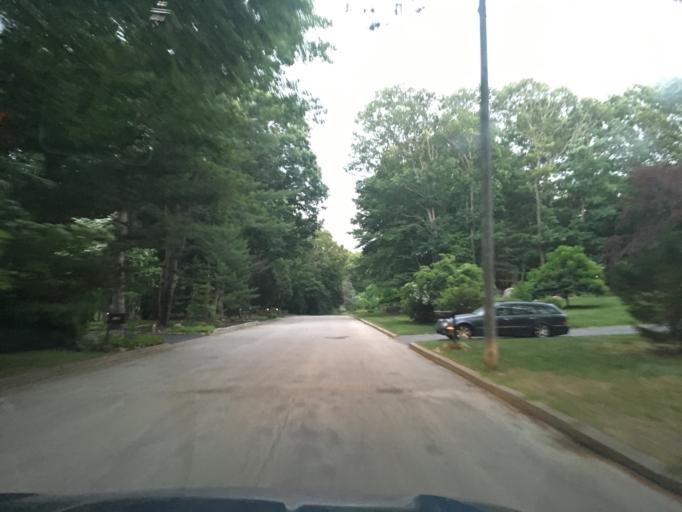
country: US
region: Rhode Island
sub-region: Washington County
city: Exeter
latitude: 41.6330
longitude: -71.5233
